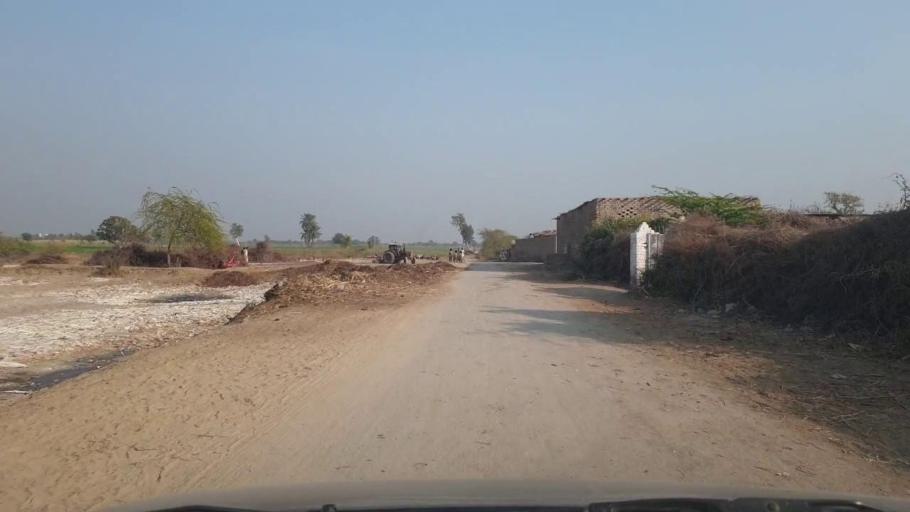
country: PK
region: Sindh
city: Digri
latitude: 25.2529
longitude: 69.1604
